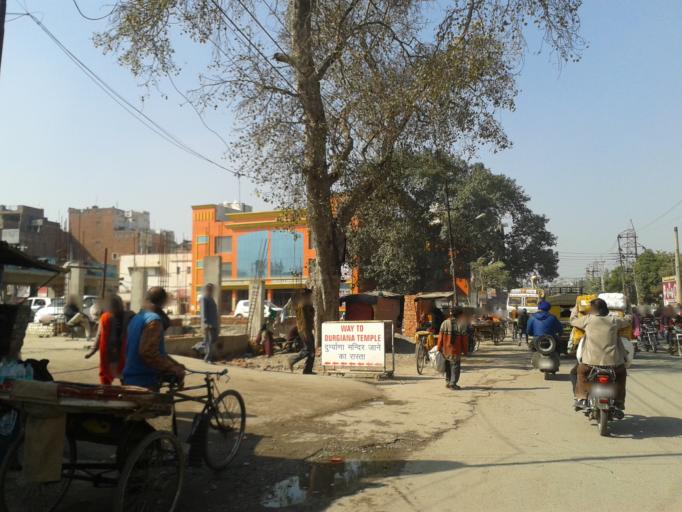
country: IN
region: Punjab
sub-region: Amritsar
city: Amritsar
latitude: 31.6285
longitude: 74.8697
